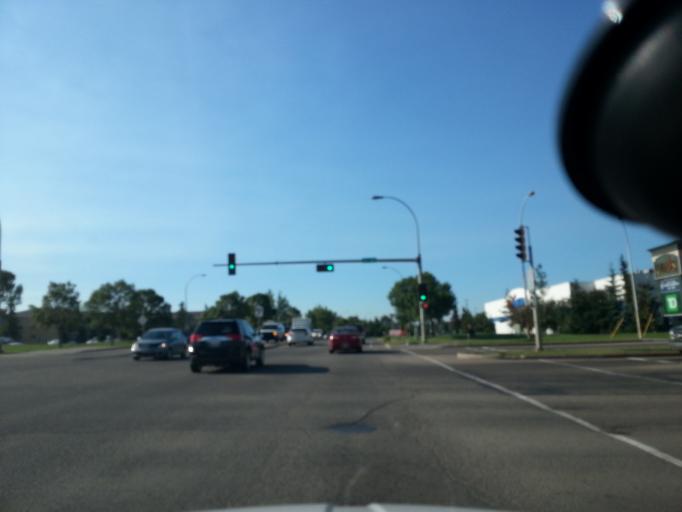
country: CA
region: Alberta
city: Edmonton
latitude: 53.5972
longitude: -113.4135
